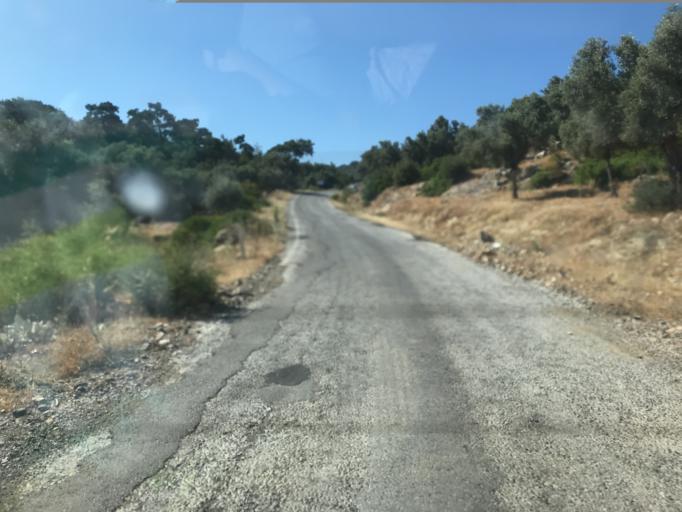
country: TR
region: Mugla
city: Selimiye
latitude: 37.3754
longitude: 27.4904
